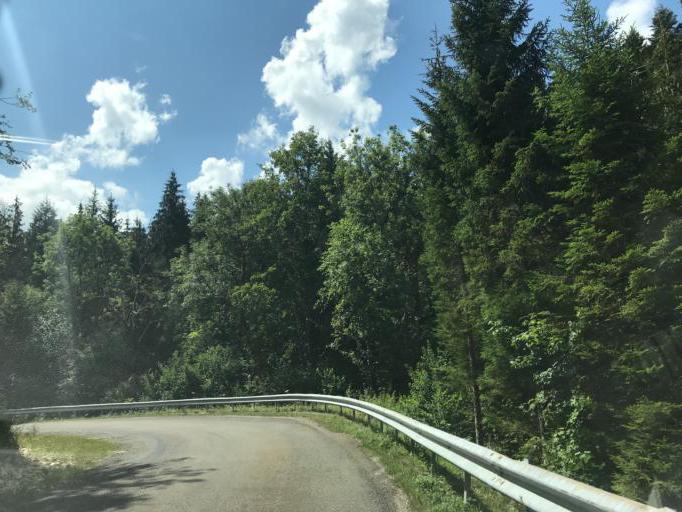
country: FR
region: Franche-Comte
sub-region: Departement du Jura
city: Moirans-en-Montagne
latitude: 46.4949
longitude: 5.7747
